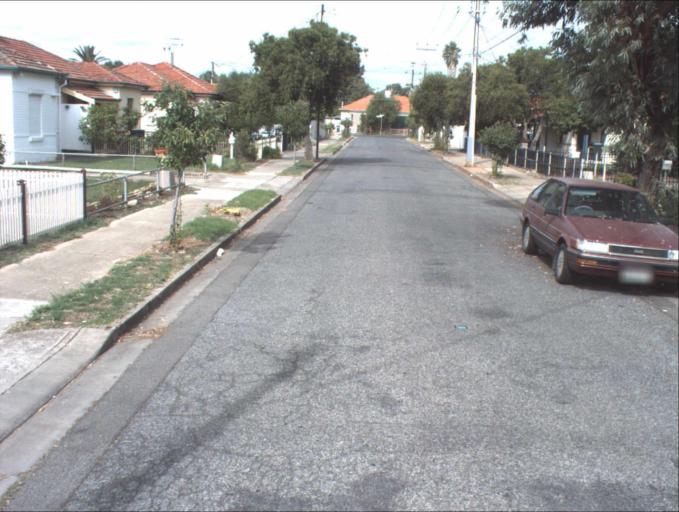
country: AU
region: South Australia
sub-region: Port Adelaide Enfield
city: Blair Athol
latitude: -34.8673
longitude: 138.5887
